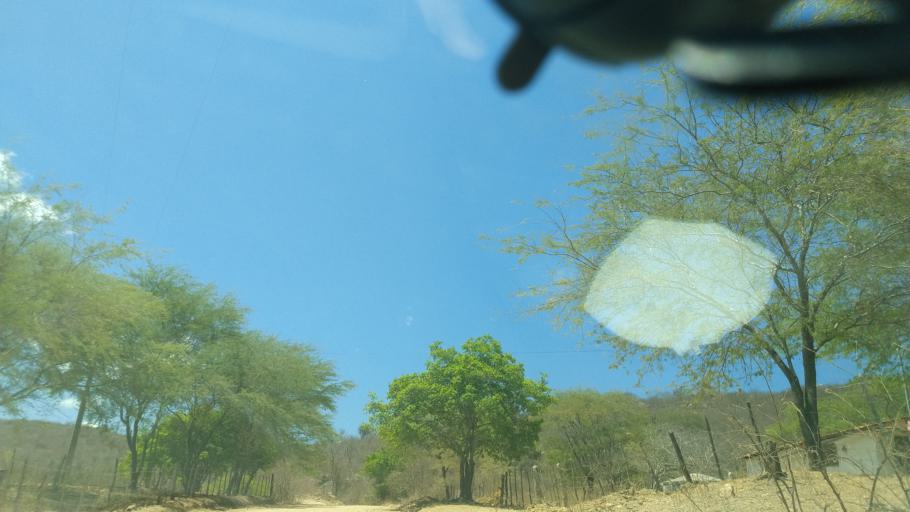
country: BR
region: Rio Grande do Norte
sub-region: Cerro Cora
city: Cerro Cora
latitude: -6.0158
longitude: -36.3119
